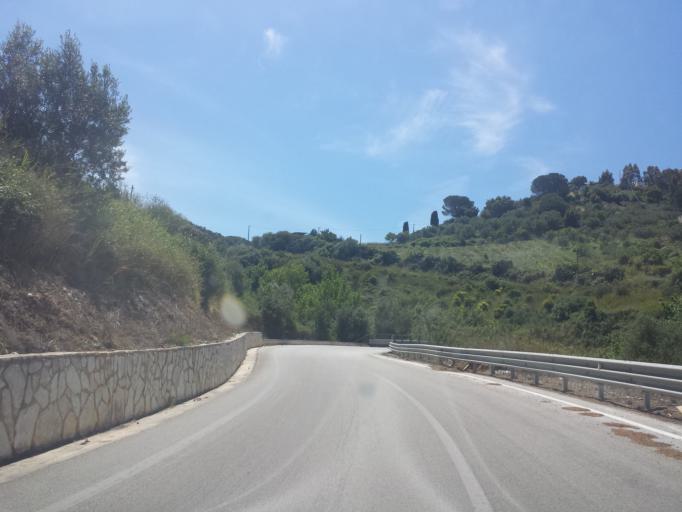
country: IT
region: Sicily
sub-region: Trapani
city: Calatafimi
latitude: 37.9574
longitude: 12.8691
